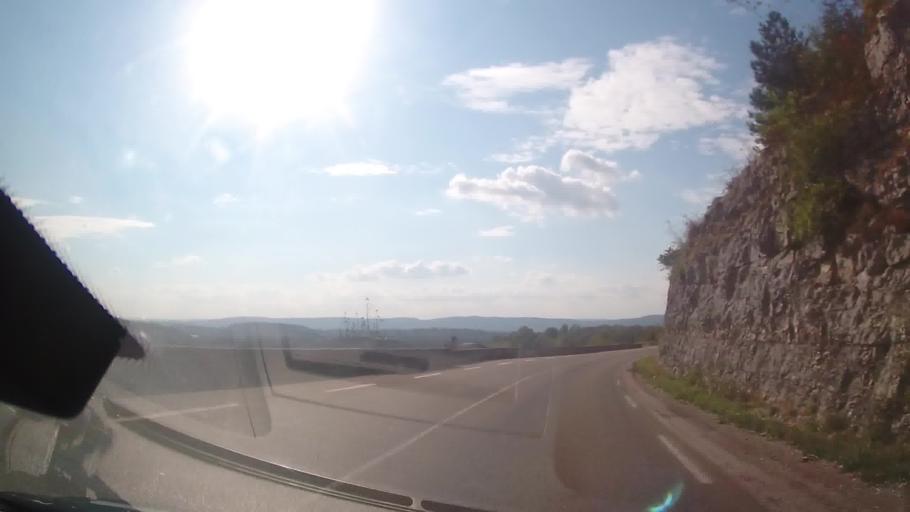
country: FR
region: Franche-Comte
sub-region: Departement du Jura
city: Clairvaux-les-Lacs
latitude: 46.5803
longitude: 5.7765
